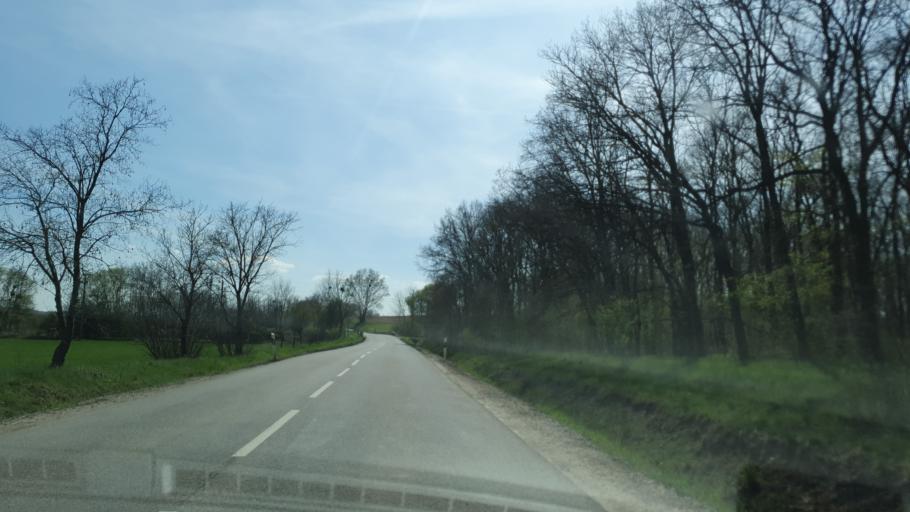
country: HU
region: Fejer
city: Pusztavam
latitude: 47.4517
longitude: 18.2389
